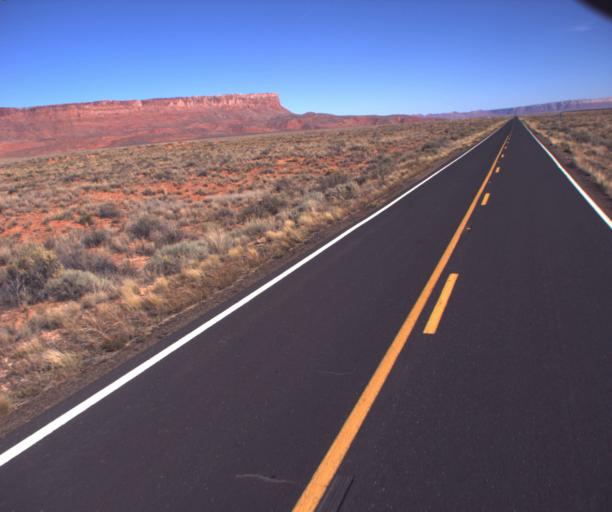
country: US
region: Arizona
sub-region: Coconino County
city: Page
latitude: 36.7031
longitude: -111.9392
